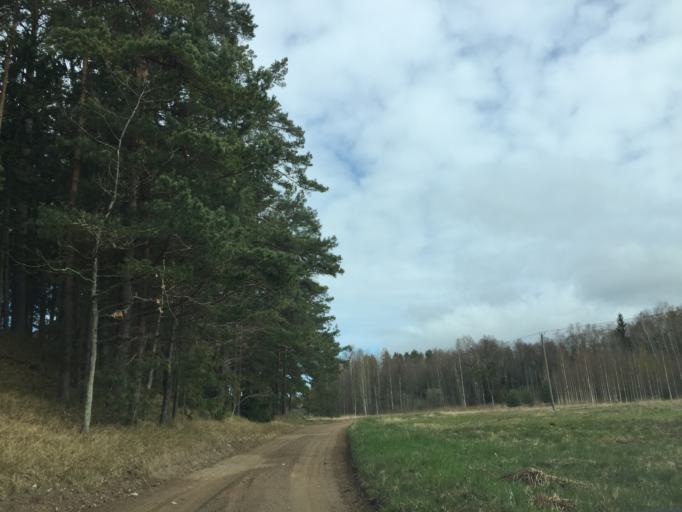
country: LV
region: Salacgrivas
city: Salacgriva
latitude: 57.5281
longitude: 24.3771
